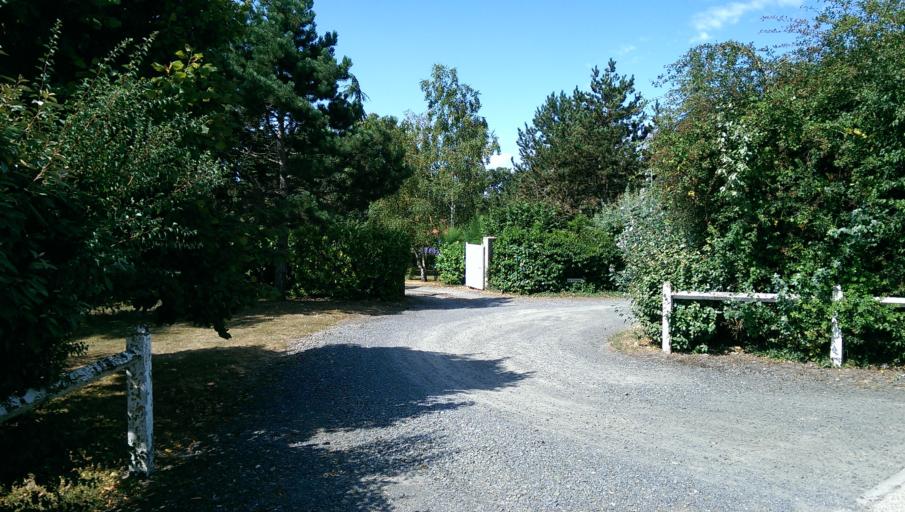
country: FR
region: Pays de la Loire
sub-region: Departement de la Loire-Atlantique
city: Clisson
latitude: 47.0856
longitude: -1.2659
